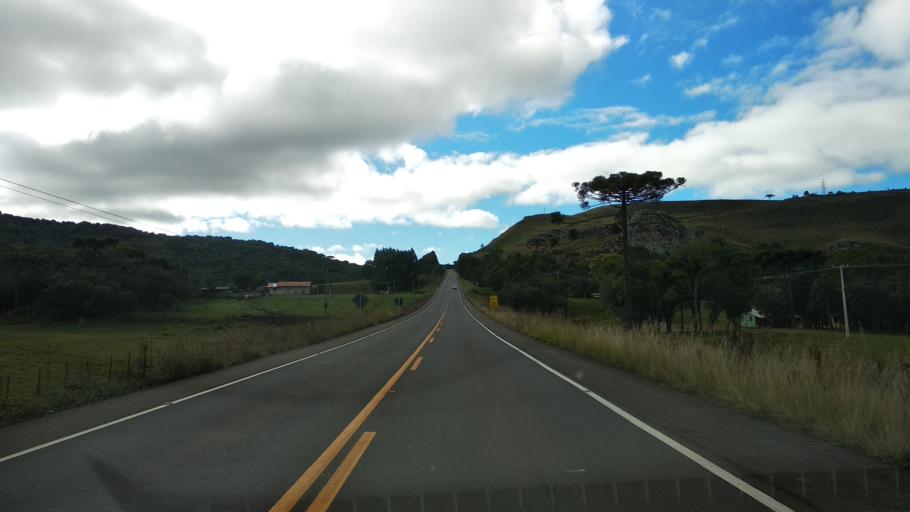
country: BR
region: Santa Catarina
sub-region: Lages
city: Lages
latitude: -27.8659
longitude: -50.2019
